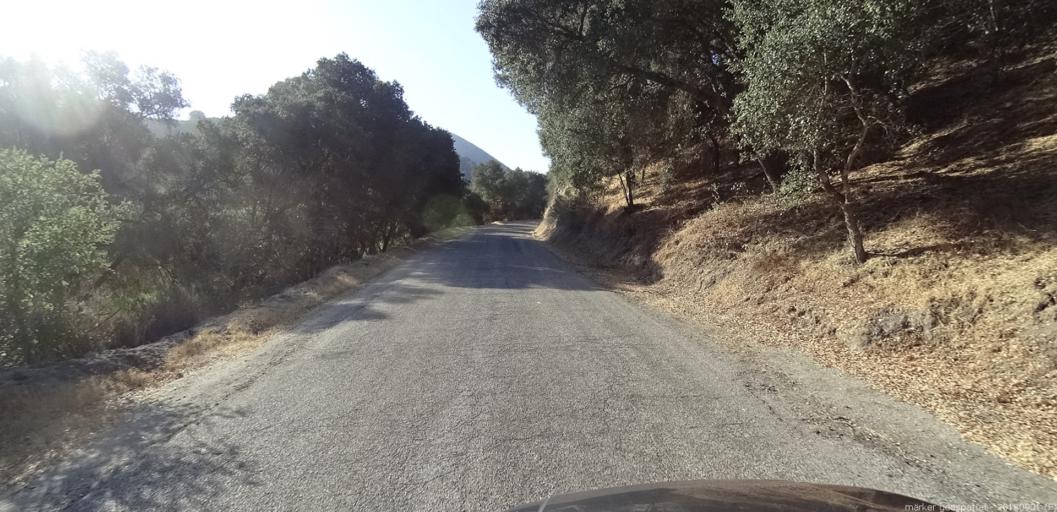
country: US
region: California
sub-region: Monterey County
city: Greenfield
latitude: 36.2357
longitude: -121.2842
